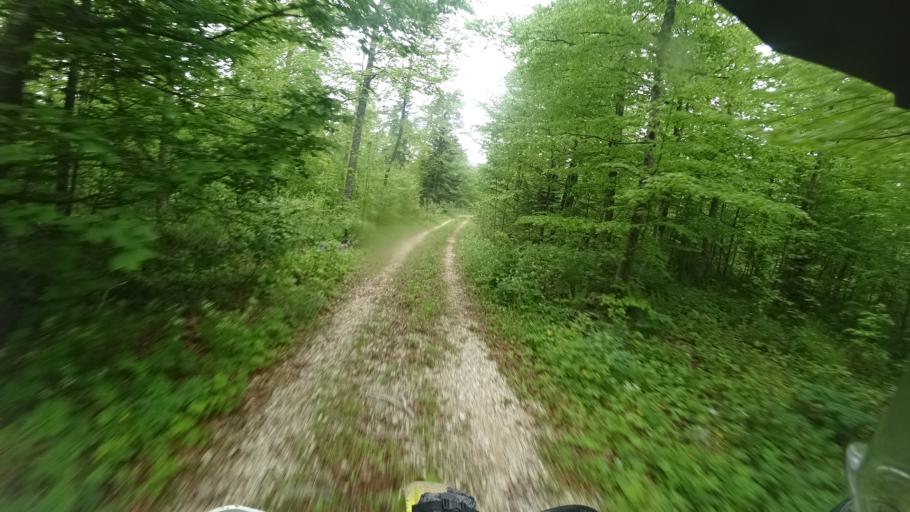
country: BA
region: Federation of Bosnia and Herzegovina
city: Orasac
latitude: 44.5659
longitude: 15.8828
